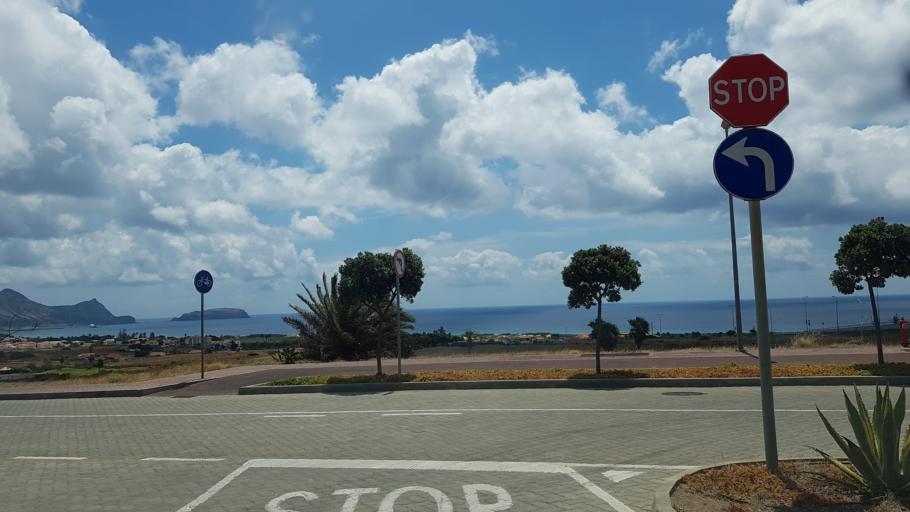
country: PT
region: Madeira
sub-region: Porto Santo
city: Vila de Porto Santo
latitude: 33.0472
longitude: -16.3635
